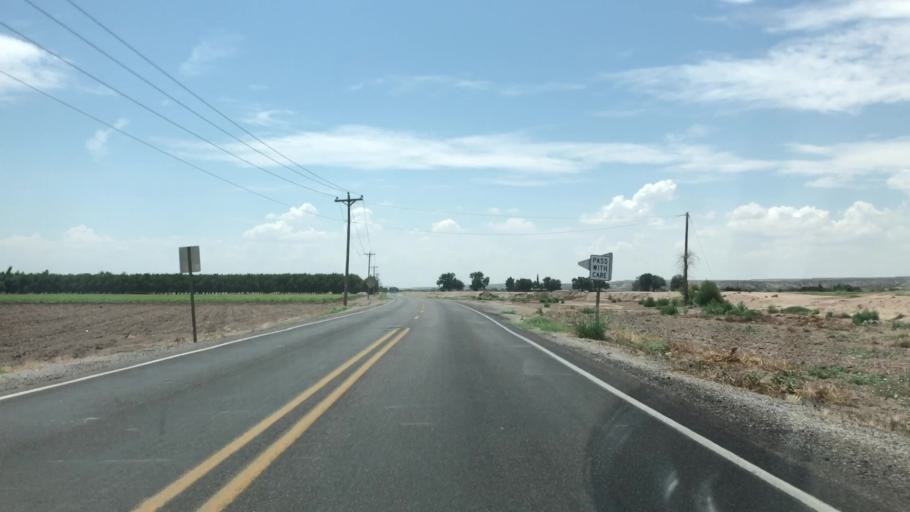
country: US
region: New Mexico
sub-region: Dona Ana County
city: Vado
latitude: 32.0813
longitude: -106.6835
